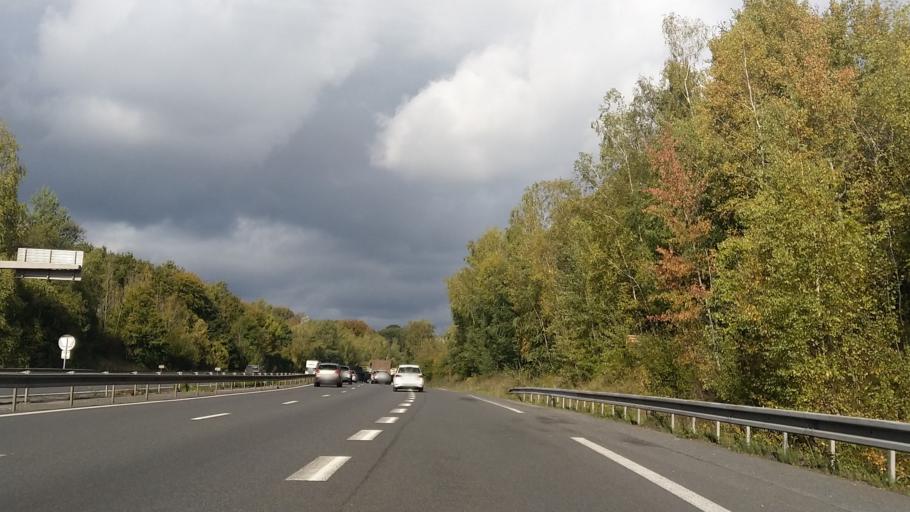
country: FR
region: Ile-de-France
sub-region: Departement du Val-d'Oise
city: L'Isle-Adam
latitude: 49.0869
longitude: 2.2579
